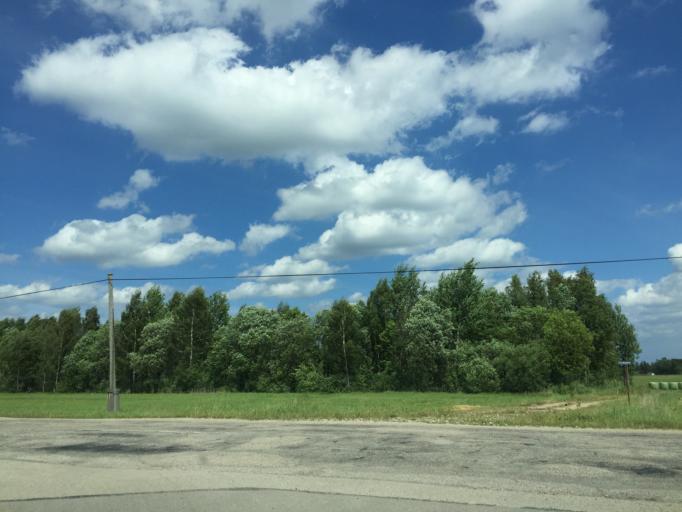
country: LV
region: Engure
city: Smarde
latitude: 56.9591
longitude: 23.3358
